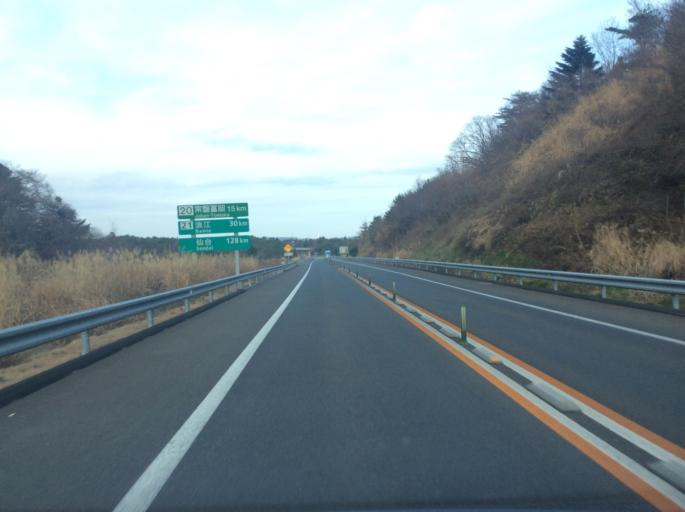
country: JP
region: Fukushima
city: Iwaki
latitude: 37.2463
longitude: 140.9882
